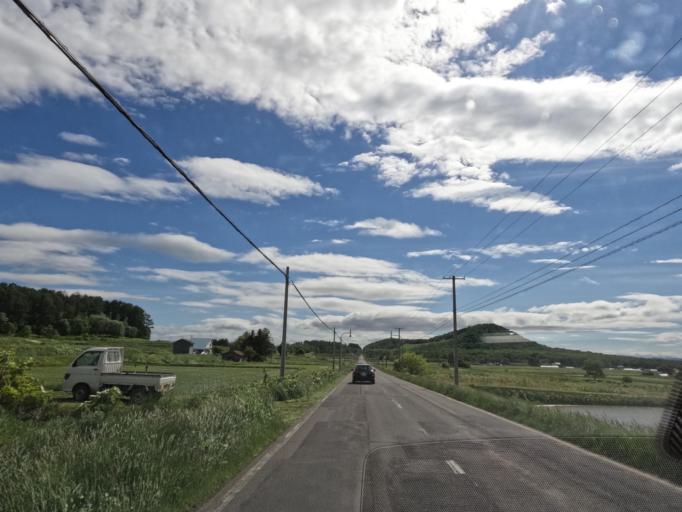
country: JP
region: Hokkaido
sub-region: Asahikawa-shi
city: Asahikawa
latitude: 43.8443
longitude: 142.5514
